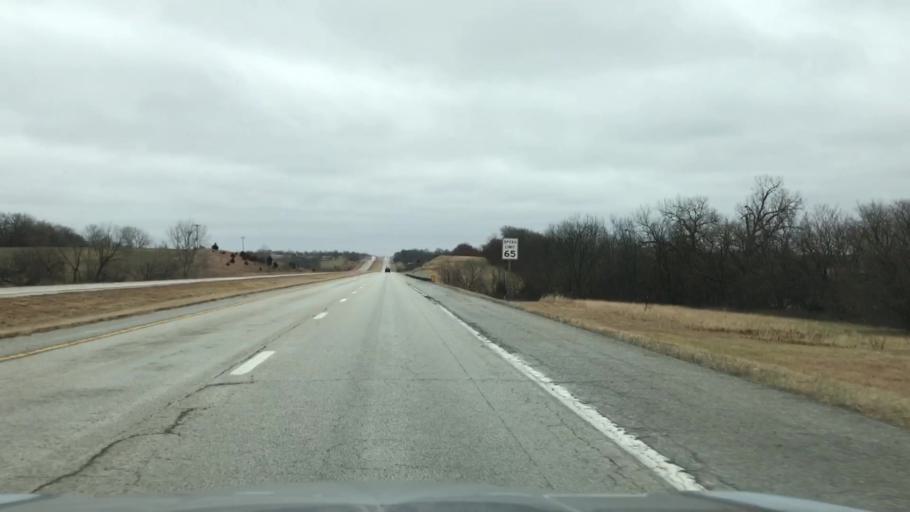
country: US
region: Missouri
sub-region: Clinton County
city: Cameron
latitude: 39.7506
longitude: -94.1294
